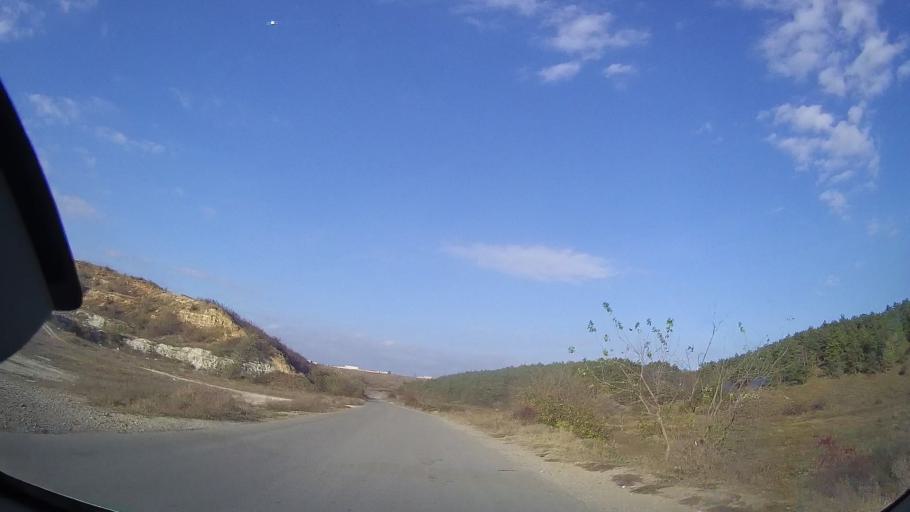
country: RO
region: Constanta
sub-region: Comuna Limanu
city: Limanu
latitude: 43.8143
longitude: 28.5173
